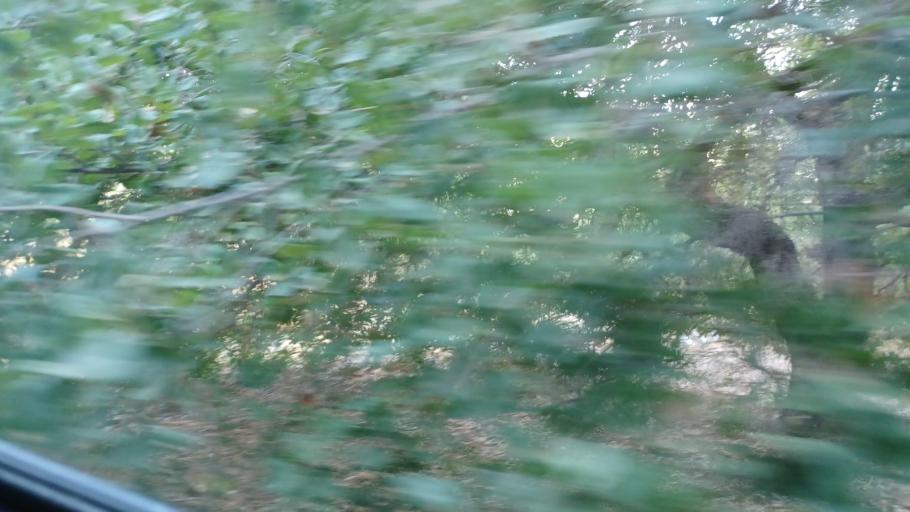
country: CY
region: Pafos
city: Tala
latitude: 34.9241
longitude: 32.4853
